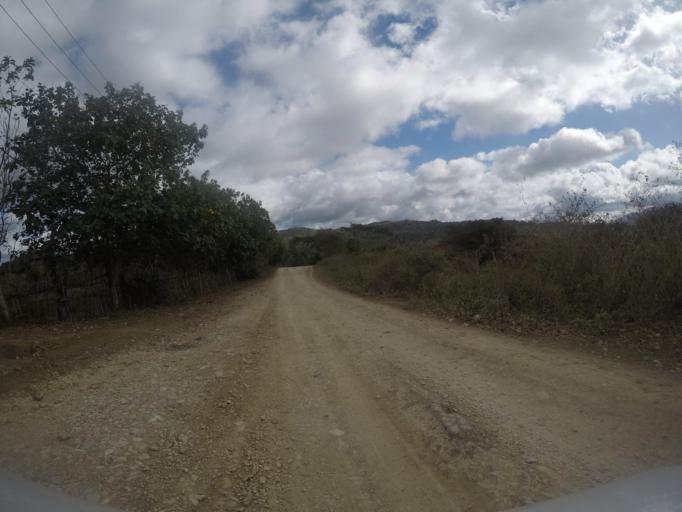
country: TL
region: Lautem
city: Lospalos
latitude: -8.5605
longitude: 126.8957
